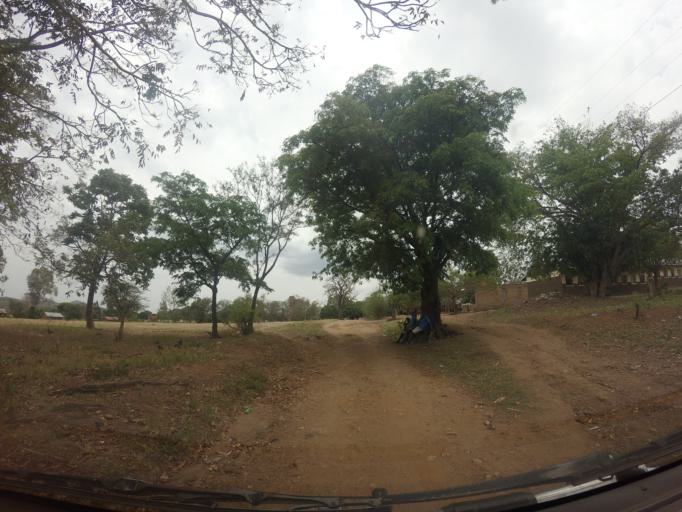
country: UG
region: Northern Region
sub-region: Arua District
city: Arua
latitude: 2.9453
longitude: 30.9398
